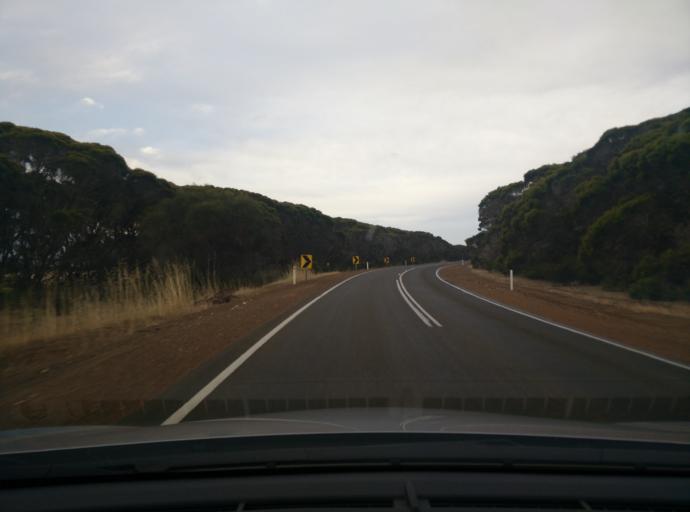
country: AU
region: South Australia
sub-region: Kangaroo Island
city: Kingscote
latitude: -35.7180
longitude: 137.5597
